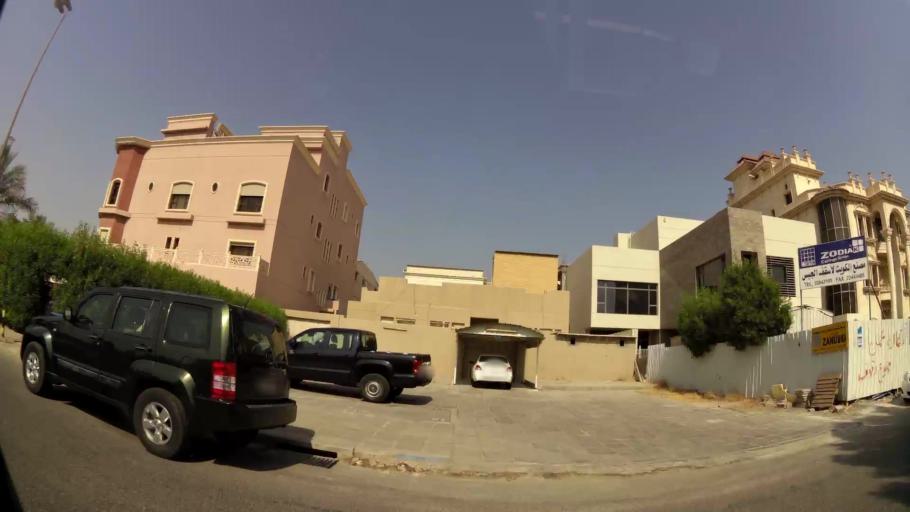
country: KW
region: Muhafazat Hawalli
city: Hawalli
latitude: 29.3494
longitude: 48.0199
